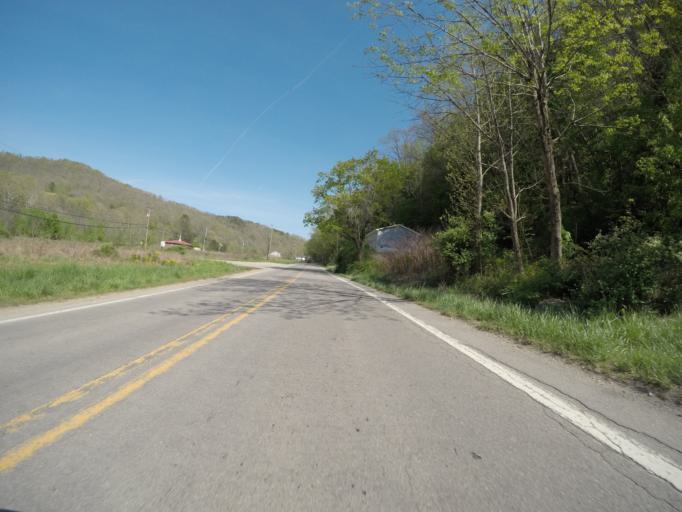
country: US
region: West Virginia
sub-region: Kanawha County
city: Clendenin
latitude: 38.5062
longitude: -81.3586
